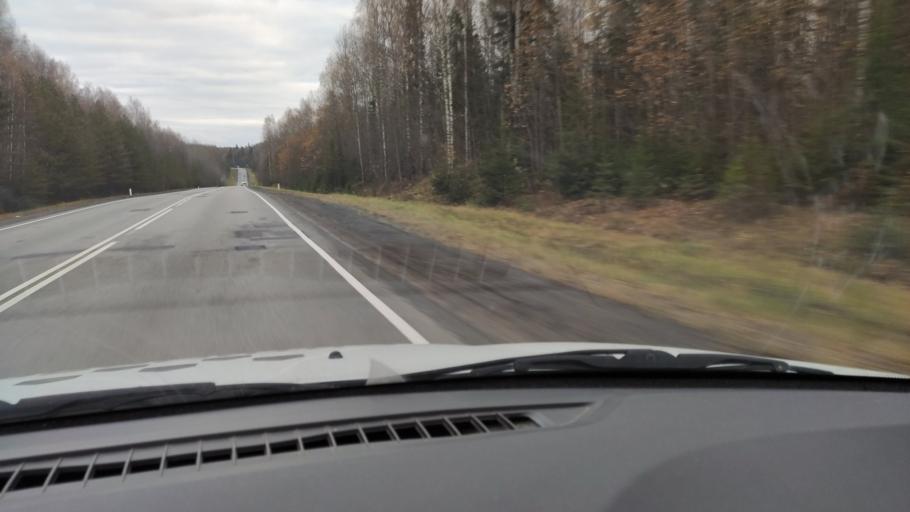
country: RU
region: Kirov
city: Chernaya Kholunitsa
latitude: 58.8606
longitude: 51.6147
